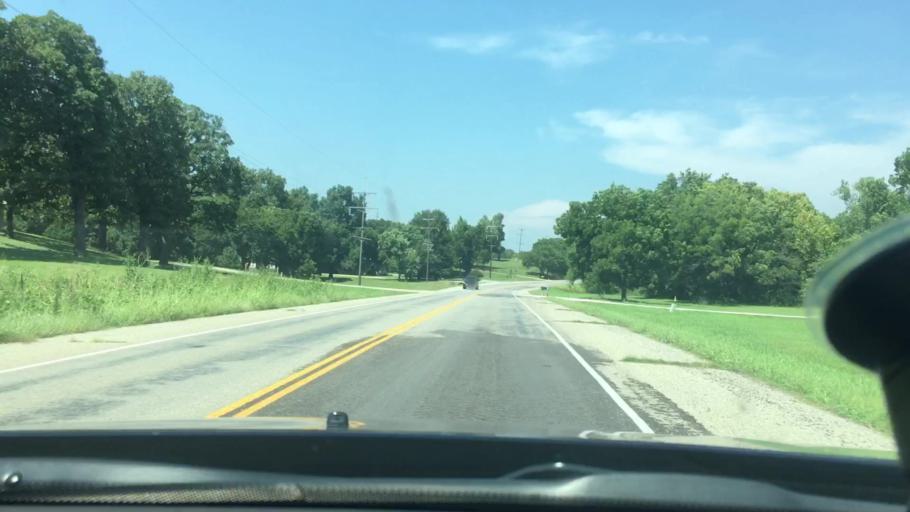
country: US
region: Oklahoma
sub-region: Pontotoc County
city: Byng
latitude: 34.8328
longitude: -96.6789
